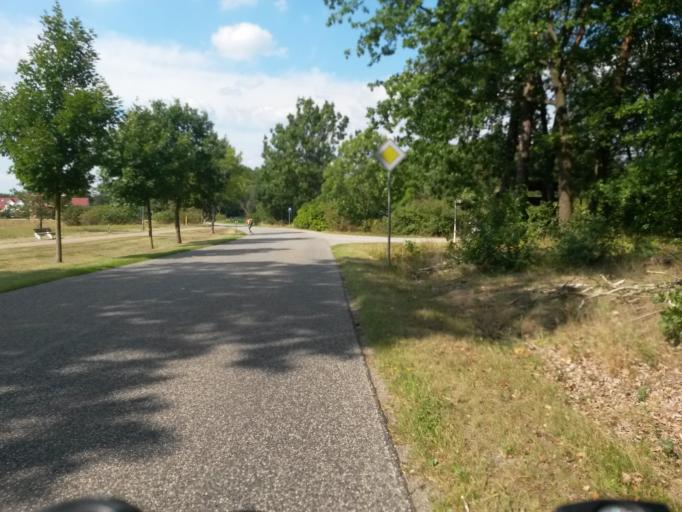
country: DE
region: Brandenburg
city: Templin
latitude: 53.1038
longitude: 13.5265
